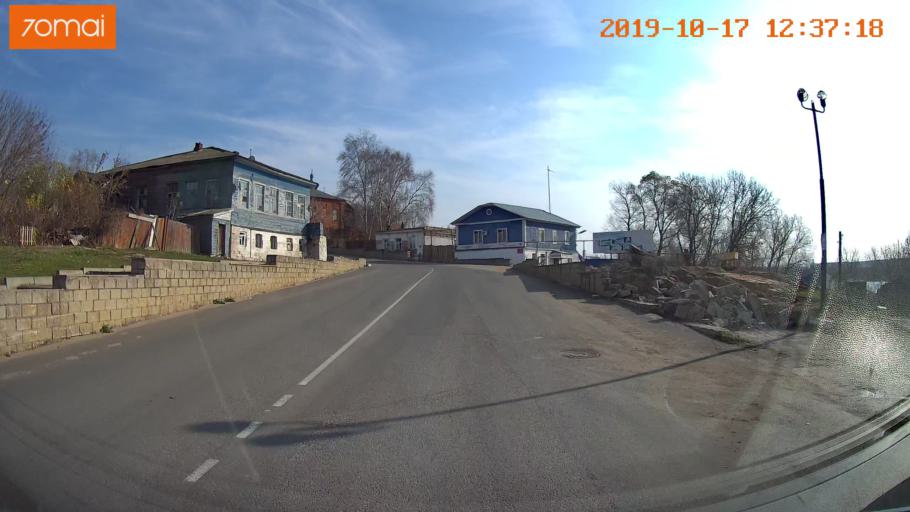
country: RU
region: Rjazan
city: Kasimov
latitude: 54.9368
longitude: 41.3853
